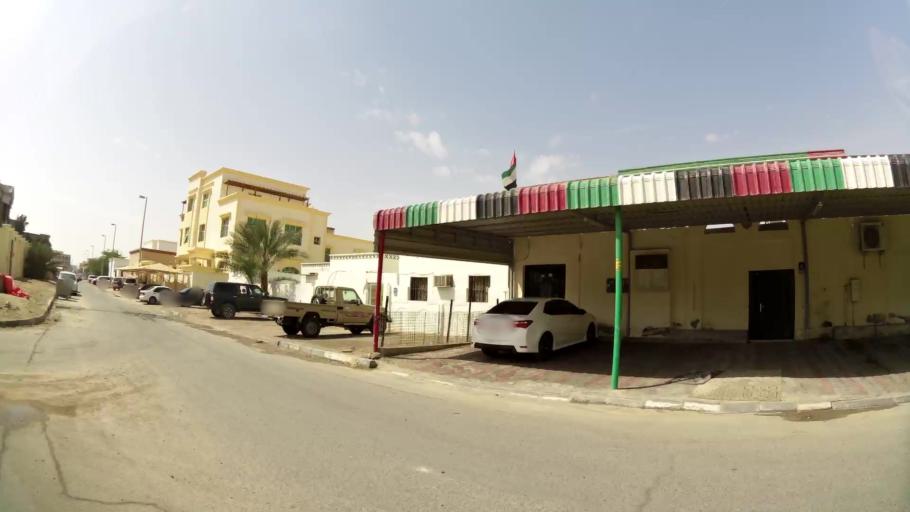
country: AE
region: Abu Dhabi
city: Abu Dhabi
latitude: 24.2990
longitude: 54.6409
